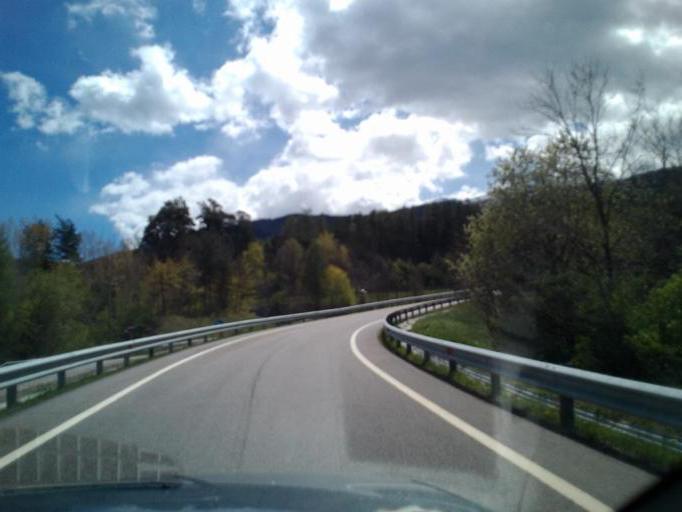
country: IT
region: Trentino-Alto Adige
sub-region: Bolzano
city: Riscone
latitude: 46.7904
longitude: 11.9538
